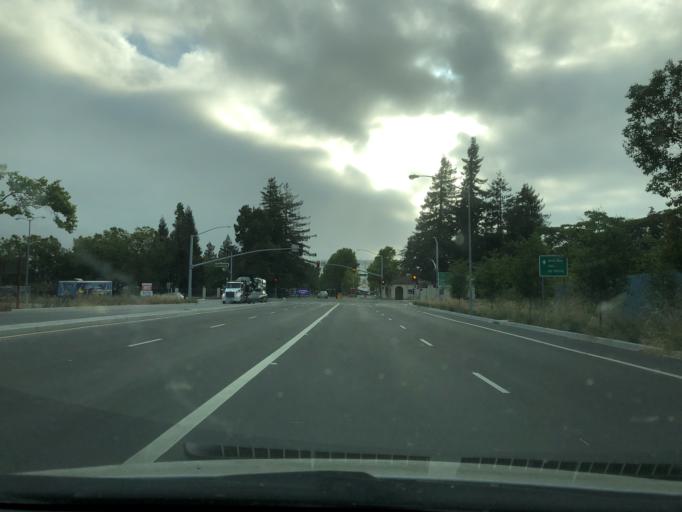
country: US
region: California
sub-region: Santa Clara County
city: Mountain View
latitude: 37.4094
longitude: -122.0647
